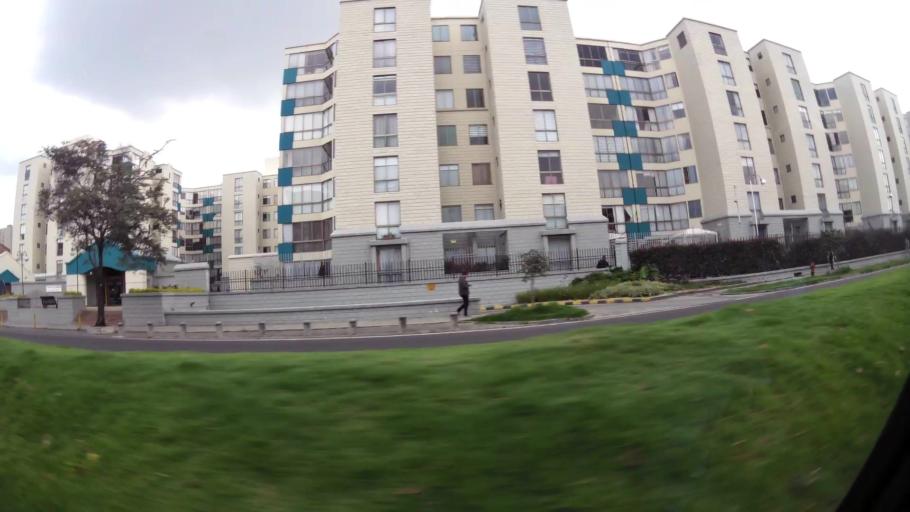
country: CO
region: Bogota D.C.
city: Barrio San Luis
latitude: 4.7284
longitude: -74.0385
